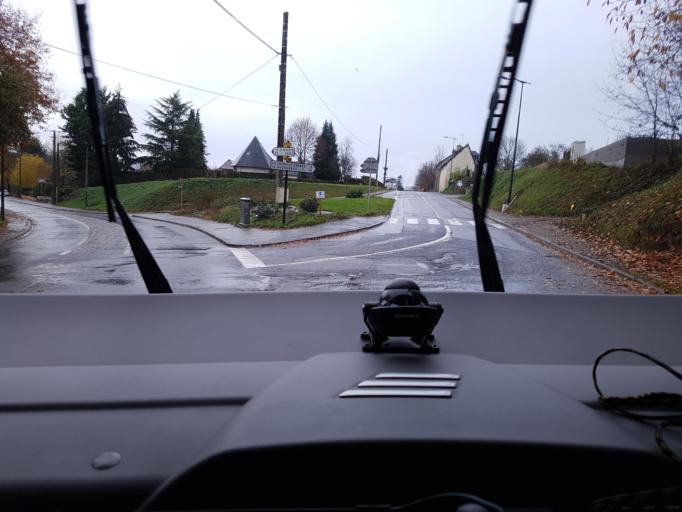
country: FR
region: Brittany
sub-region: Departement d'Ille-et-Vilaine
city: Vitre
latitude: 48.1268
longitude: -1.1977
